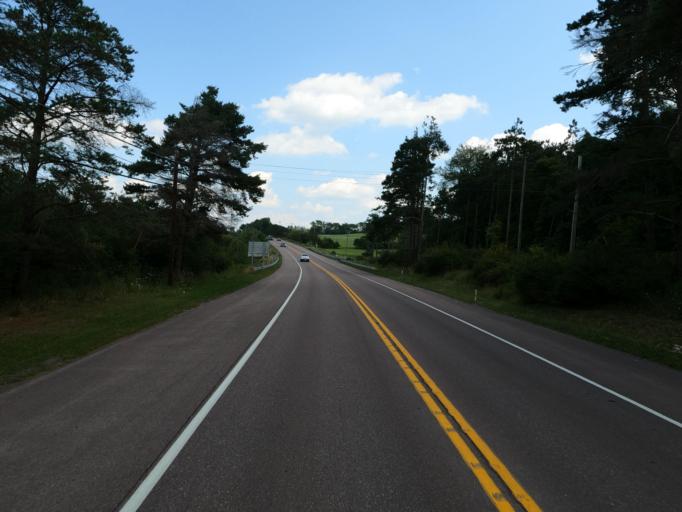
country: US
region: Maryland
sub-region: Garrett County
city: Oakland
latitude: 39.4278
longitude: -79.3889
